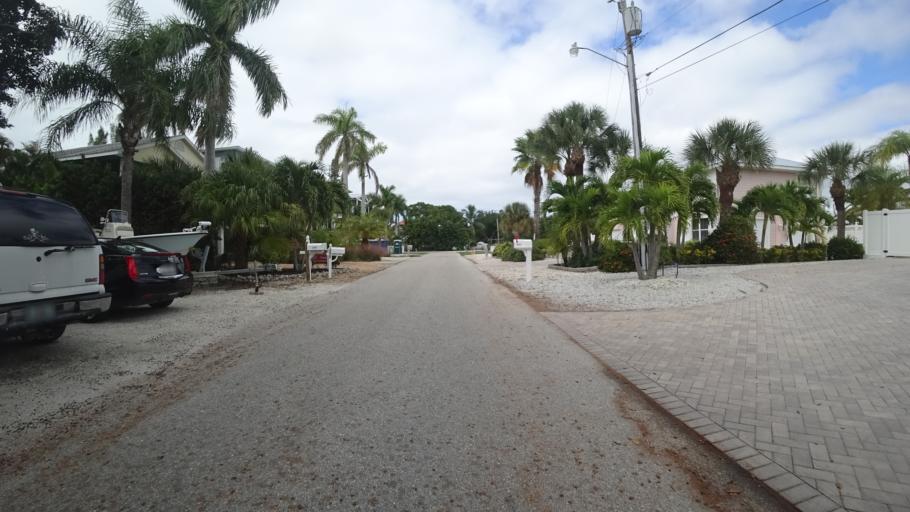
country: US
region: Florida
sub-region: Manatee County
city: Bradenton Beach
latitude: 27.4788
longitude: -82.7014
